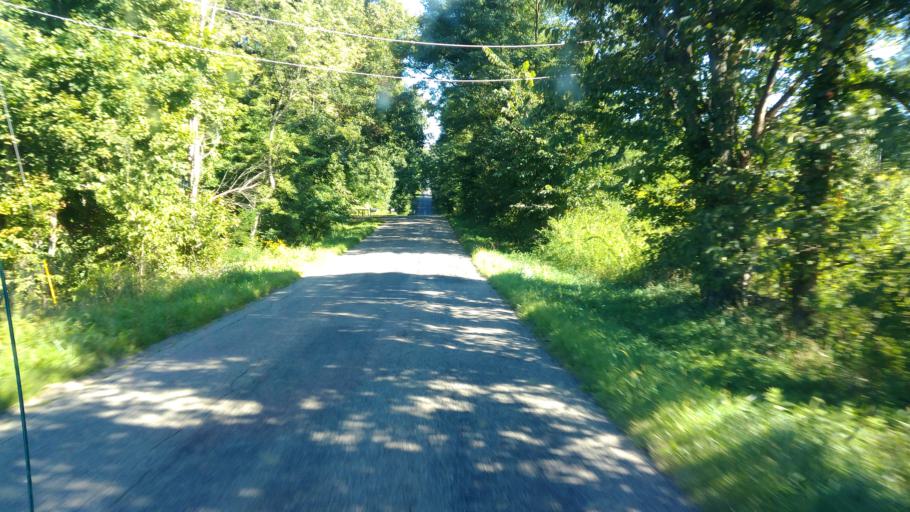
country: US
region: Ohio
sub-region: Knox County
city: Mount Vernon
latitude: 40.4536
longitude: -82.4350
